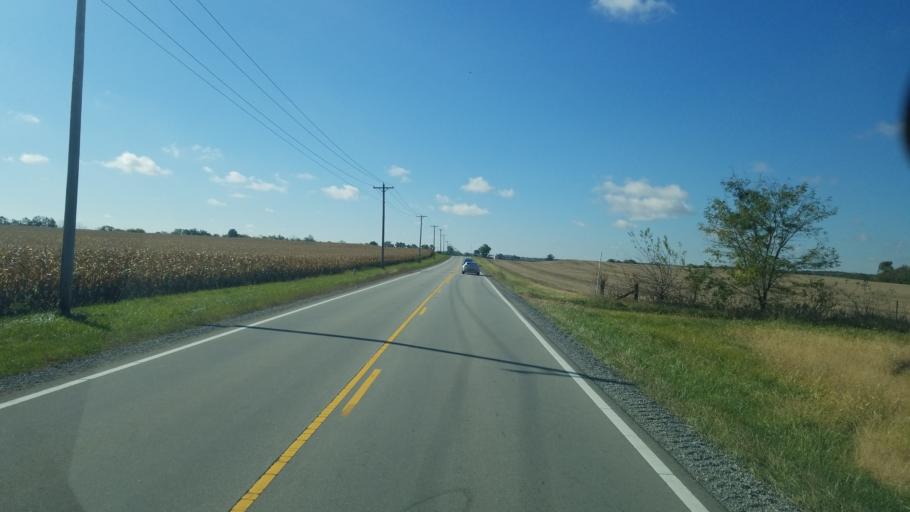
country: US
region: Ohio
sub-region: Highland County
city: Leesburg
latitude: 39.4144
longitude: -83.5237
